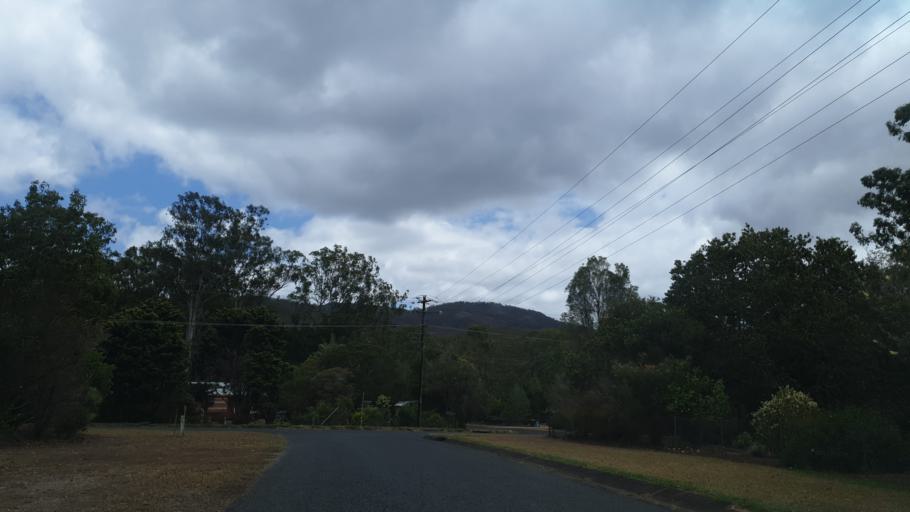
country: AU
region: Queensland
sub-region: Tablelands
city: Tolga
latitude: -17.2072
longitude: 145.4387
